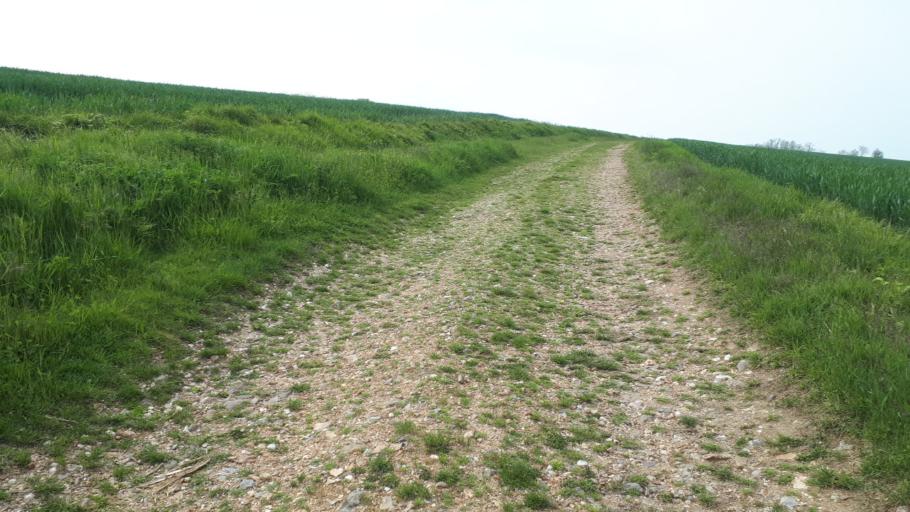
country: FR
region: Centre
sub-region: Departement du Loir-et-Cher
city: Lunay
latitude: 47.8227
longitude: 0.9423
